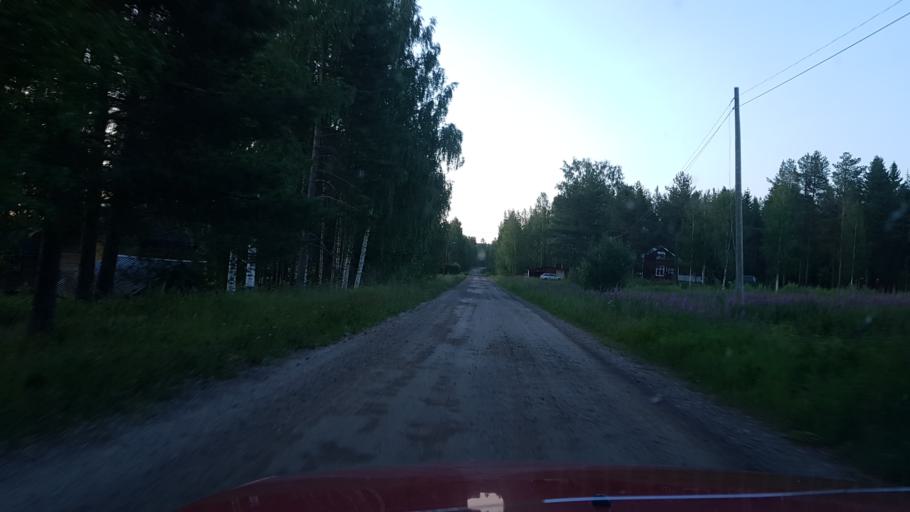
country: SE
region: Norrbotten
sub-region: Alvsbyns Kommun
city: AElvsbyn
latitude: 65.7003
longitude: 20.6790
